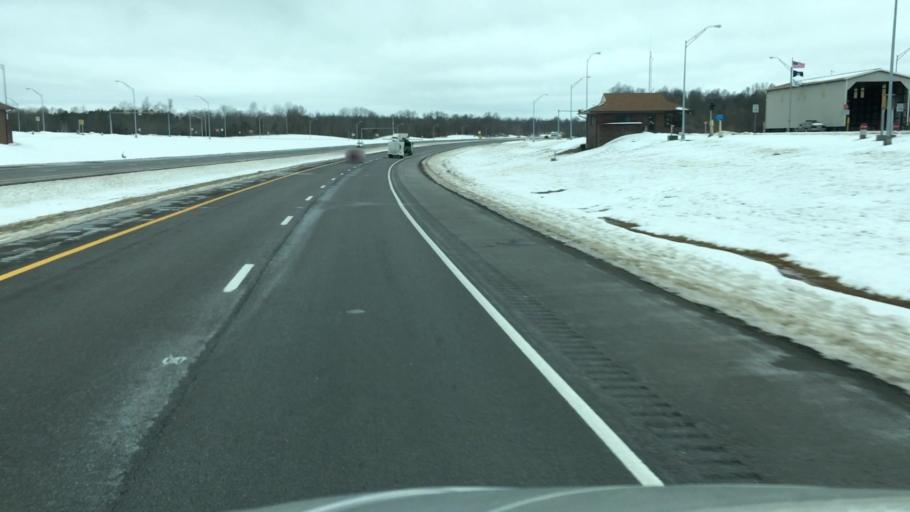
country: US
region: Kentucky
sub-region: Lyon County
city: Eddyville
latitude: 37.0611
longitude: -88.1822
